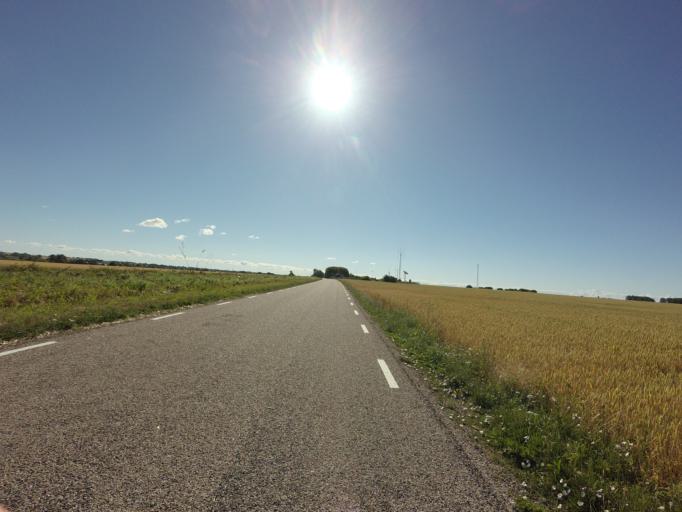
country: SE
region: Skane
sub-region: Trelleborgs Kommun
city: Skare
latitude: 55.3905
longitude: 13.0640
